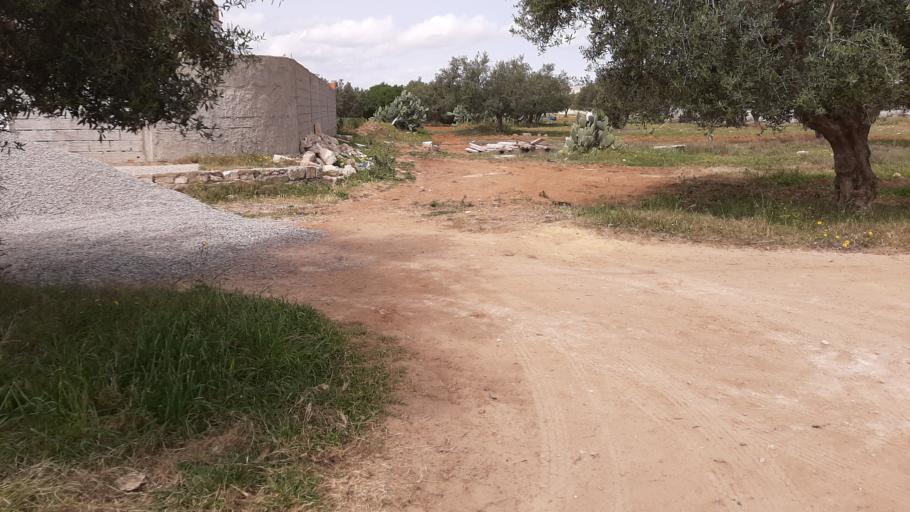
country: TN
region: Al Munastir
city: Qusaybat al Madyuni
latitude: 35.6898
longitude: 10.8342
